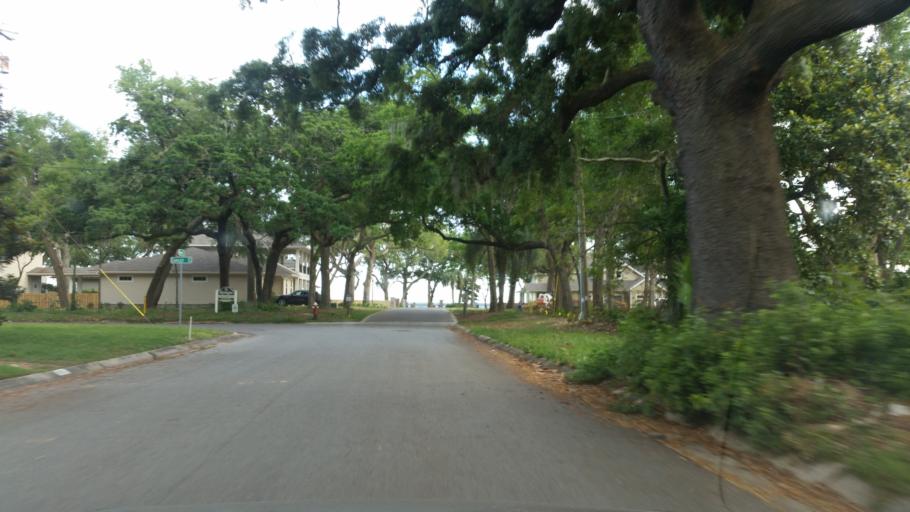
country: US
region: Florida
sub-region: Escambia County
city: East Pensacola Heights
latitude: 30.4228
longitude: -87.1854
